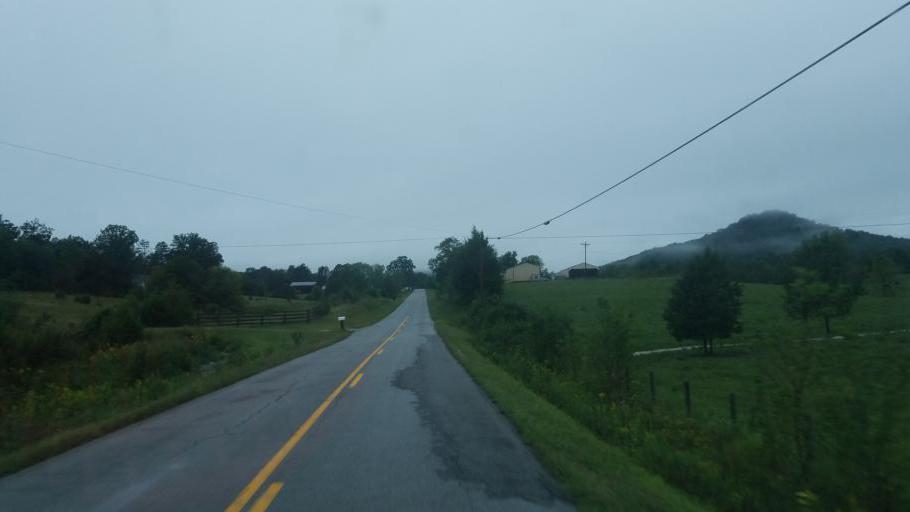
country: US
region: Kentucky
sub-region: Fleming County
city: Flemingsburg
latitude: 38.4032
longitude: -83.6210
